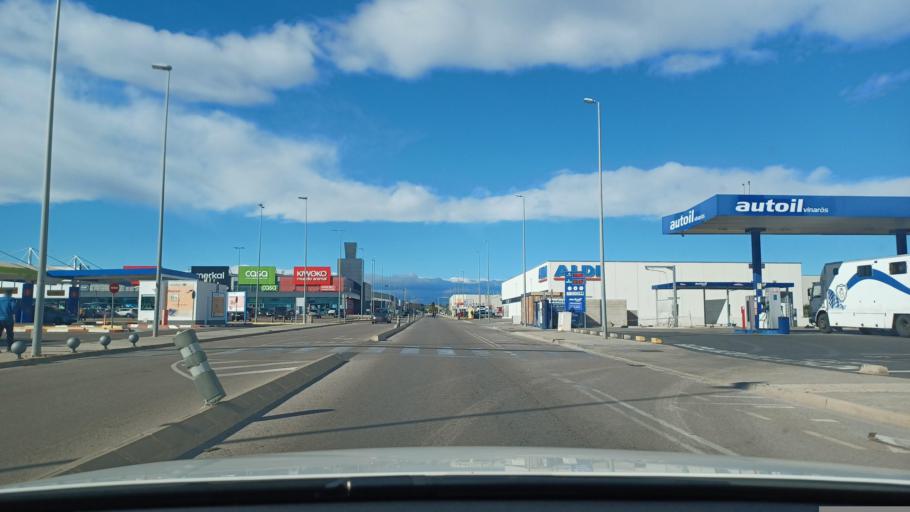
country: ES
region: Valencia
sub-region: Provincia de Castello
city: Vinaros
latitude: 40.4550
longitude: 0.4526
